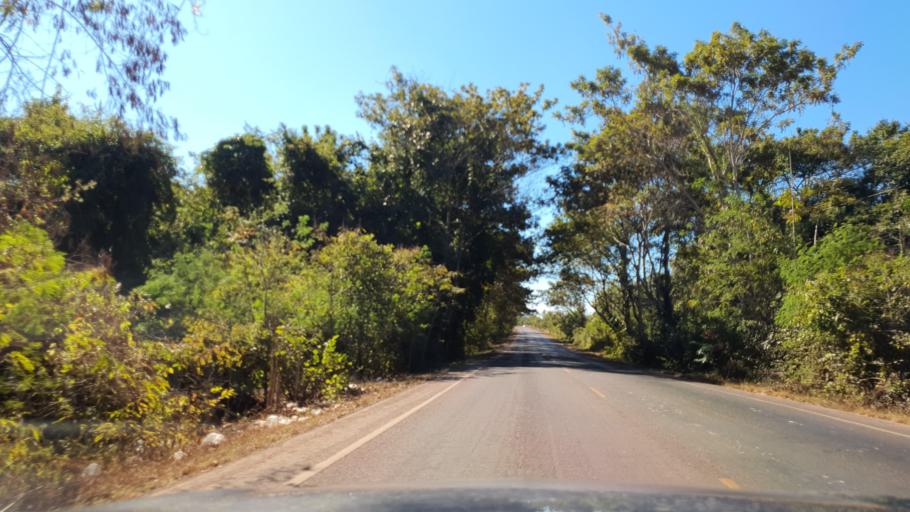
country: TH
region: Nakhon Phanom
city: Si Songkhram
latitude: 17.7544
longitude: 104.2863
